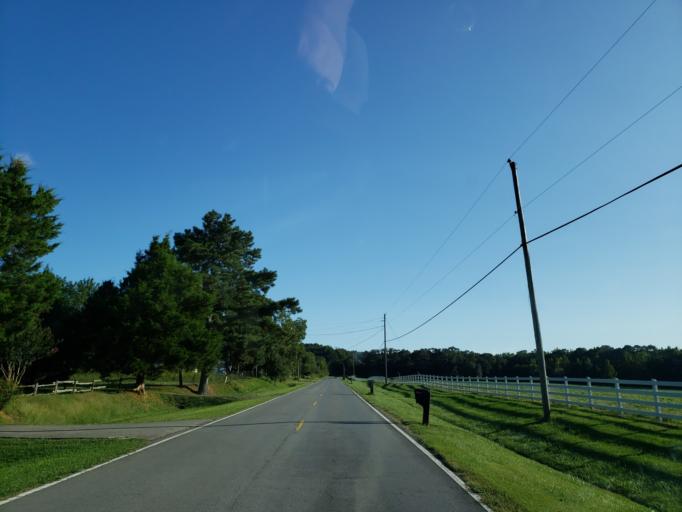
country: US
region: Georgia
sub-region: Bartow County
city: Rydal
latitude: 34.3081
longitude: -84.7741
